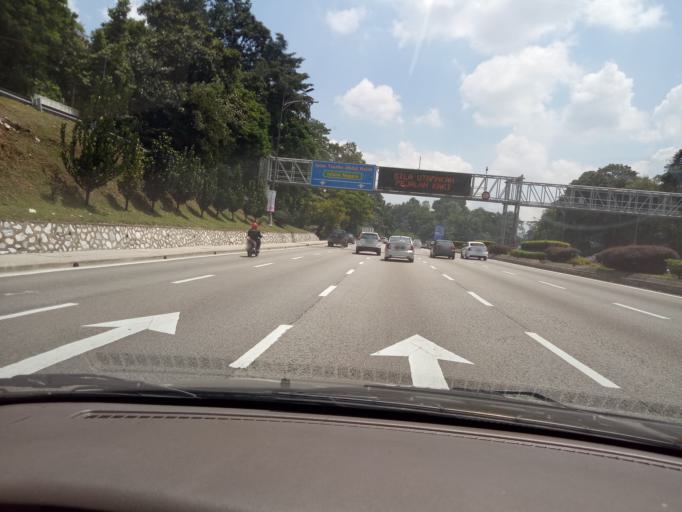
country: MY
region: Kuala Lumpur
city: Kuala Lumpur
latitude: 3.1410
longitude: 101.6802
